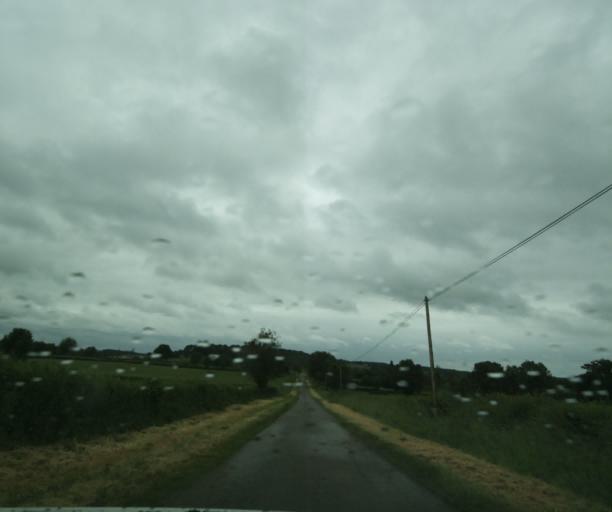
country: FR
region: Bourgogne
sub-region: Departement de Saone-et-Loire
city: Charolles
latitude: 46.4831
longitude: 4.2726
